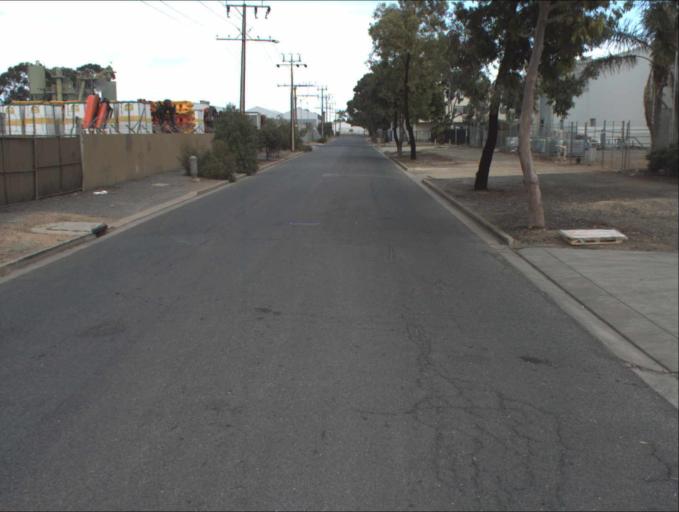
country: AU
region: South Australia
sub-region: Port Adelaide Enfield
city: Enfield
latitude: -34.8452
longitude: 138.5925
